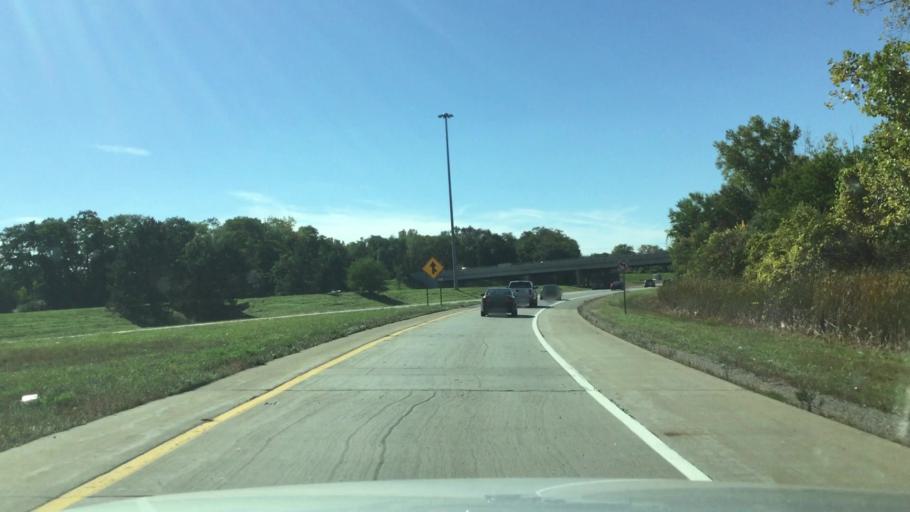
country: US
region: Michigan
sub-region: Wayne County
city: Plymouth
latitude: 42.3875
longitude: -83.4411
